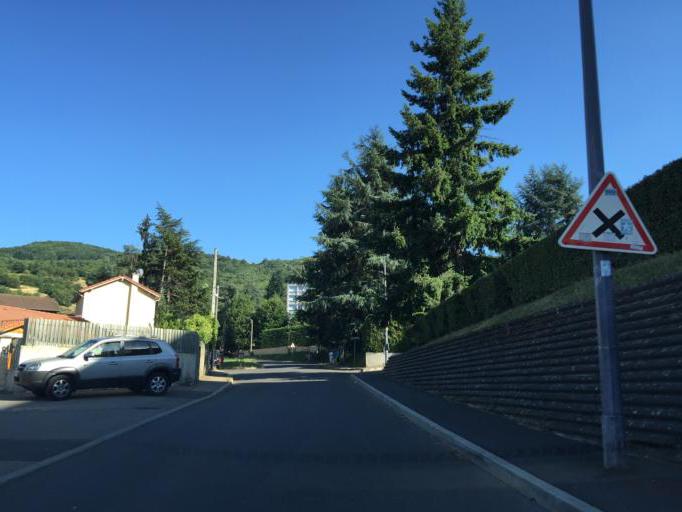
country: FR
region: Rhone-Alpes
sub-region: Departement de la Loire
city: Saint-Jean-Bonnefonds
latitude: 45.4328
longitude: 4.4424
